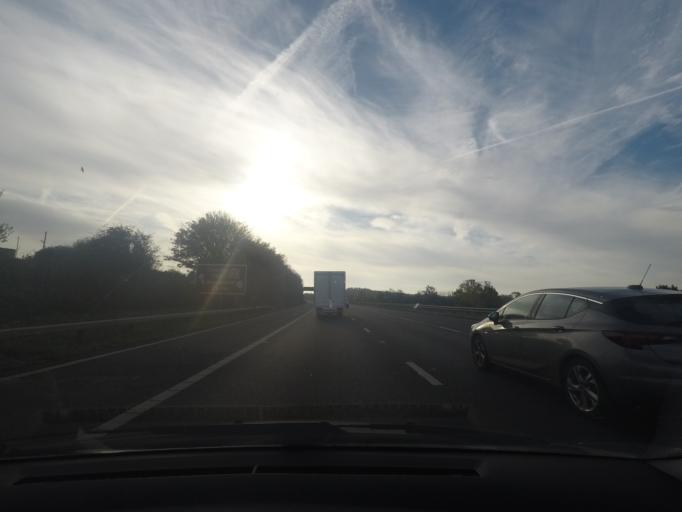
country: GB
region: England
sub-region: Barnsley
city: Dodworth
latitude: 53.5624
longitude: -1.5370
